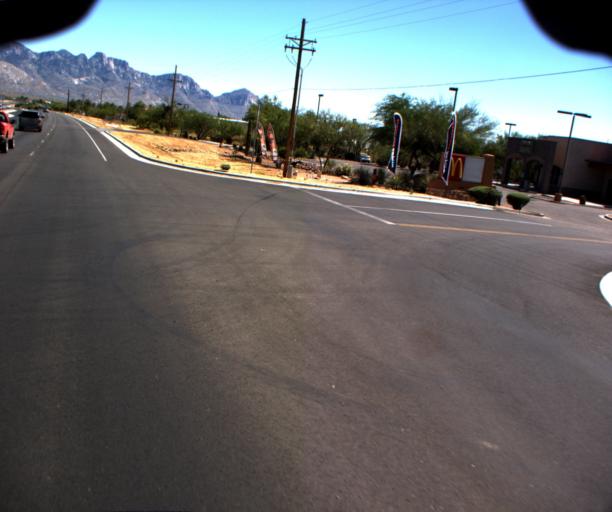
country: US
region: Arizona
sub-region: Pima County
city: Catalina
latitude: 32.4945
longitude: -110.9258
